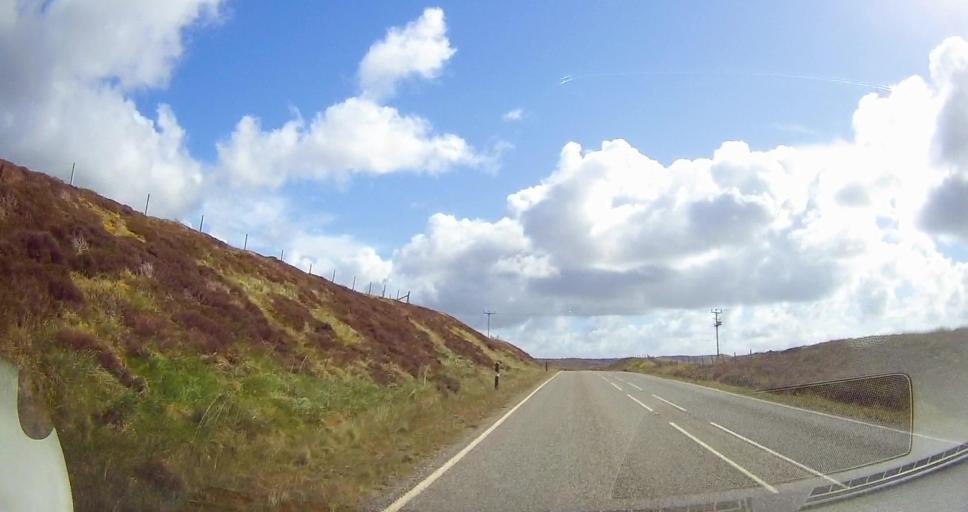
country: GB
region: Scotland
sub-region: Shetland Islands
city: Lerwick
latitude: 60.4707
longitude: -1.4068
